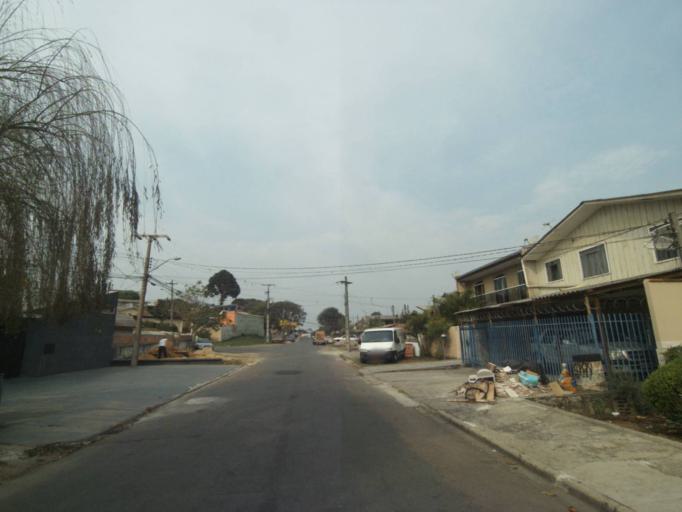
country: BR
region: Parana
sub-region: Sao Jose Dos Pinhais
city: Sao Jose dos Pinhais
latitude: -25.5221
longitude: -49.2763
